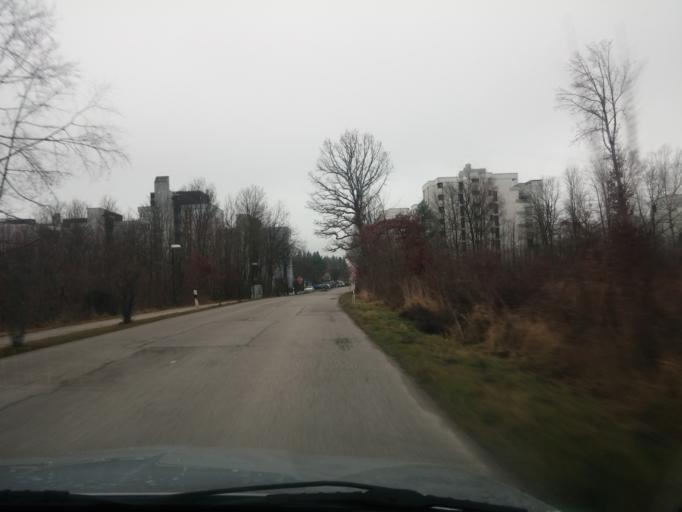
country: DE
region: Bavaria
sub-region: Upper Bavaria
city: Putzbrunn
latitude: 48.0768
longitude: 11.6934
